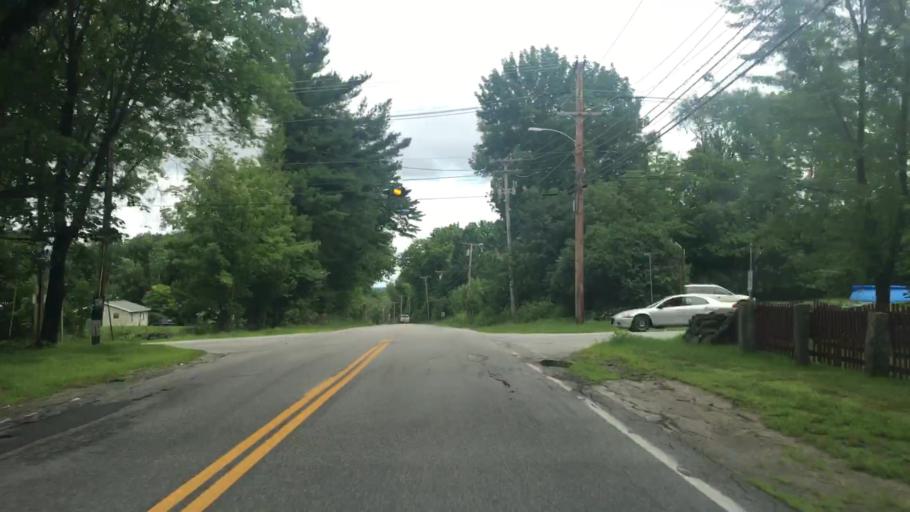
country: US
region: Maine
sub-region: York County
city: Limerick
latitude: 43.6790
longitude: -70.7870
